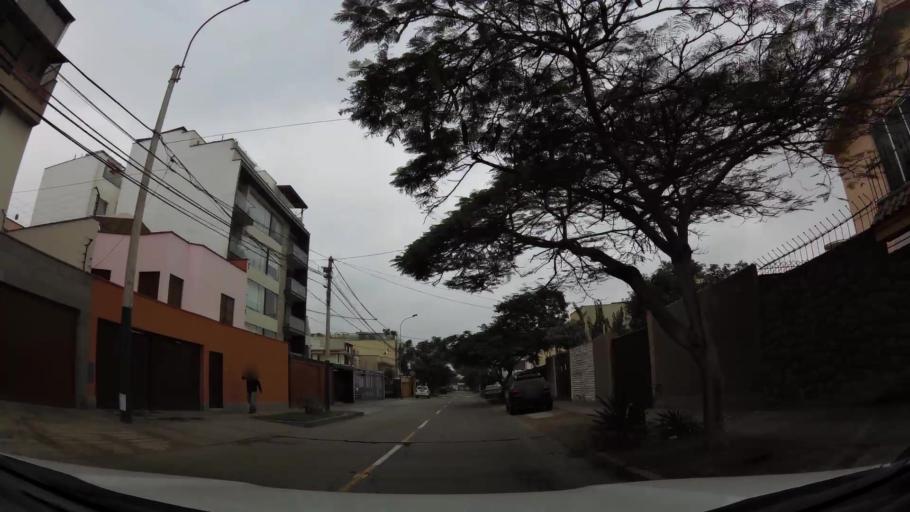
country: PE
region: Lima
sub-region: Lima
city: Surco
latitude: -12.1182
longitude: -76.9926
